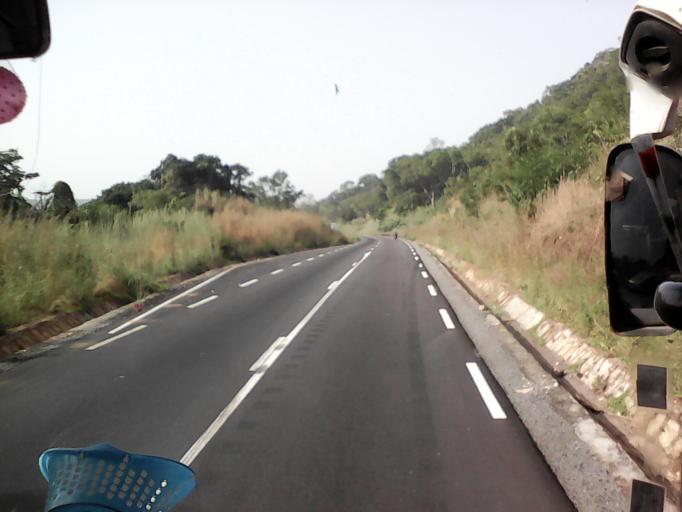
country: TG
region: Kara
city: Bafilo
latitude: 9.2432
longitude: 1.2132
